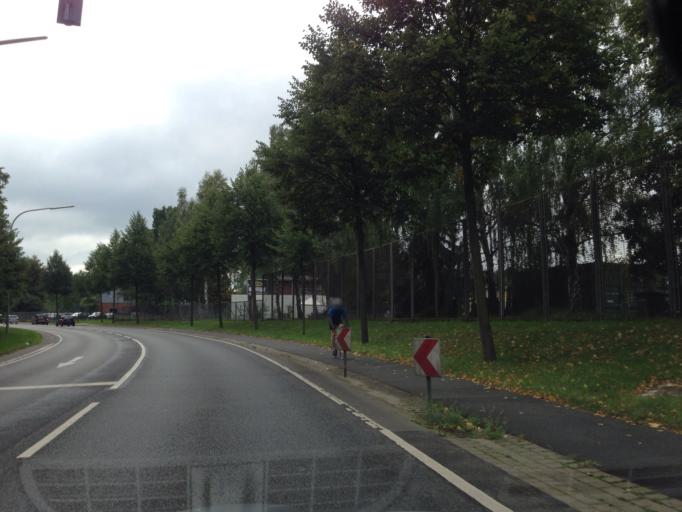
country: DE
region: Lower Saxony
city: Lueneburg
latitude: 53.2596
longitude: 10.4189
